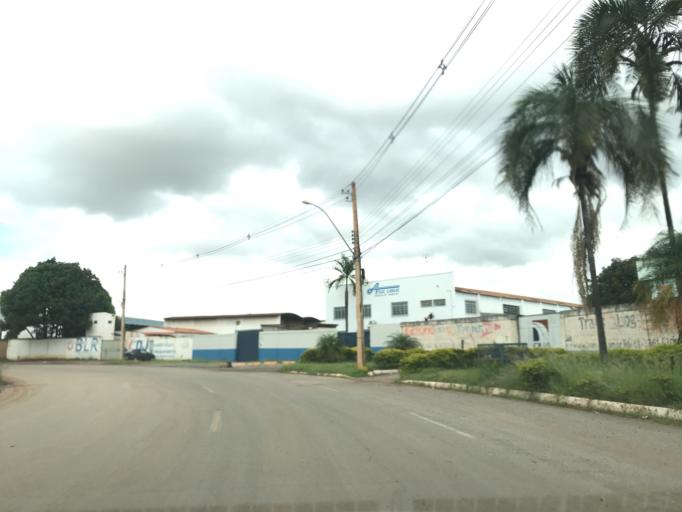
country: BR
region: Federal District
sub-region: Brasilia
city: Brasilia
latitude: -15.7899
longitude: -47.9883
